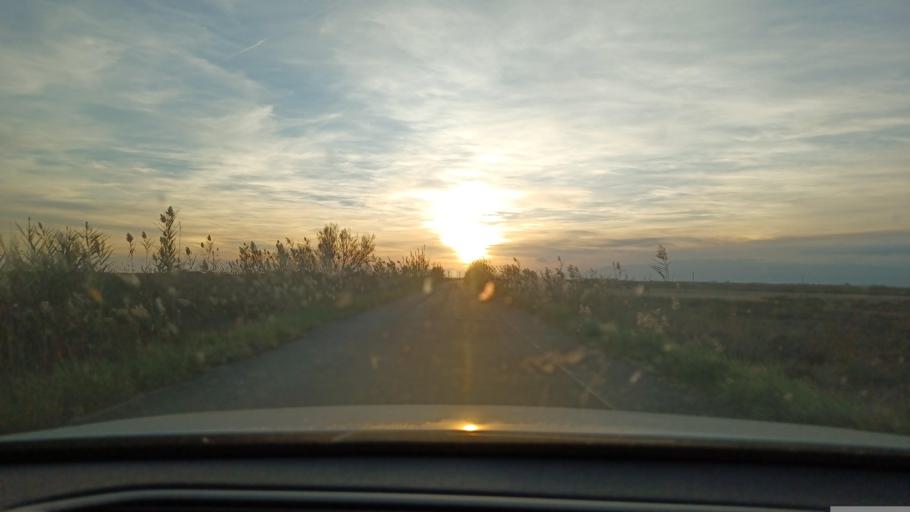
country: ES
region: Catalonia
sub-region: Provincia de Tarragona
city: Deltebre
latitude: 40.6540
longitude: 0.7694
